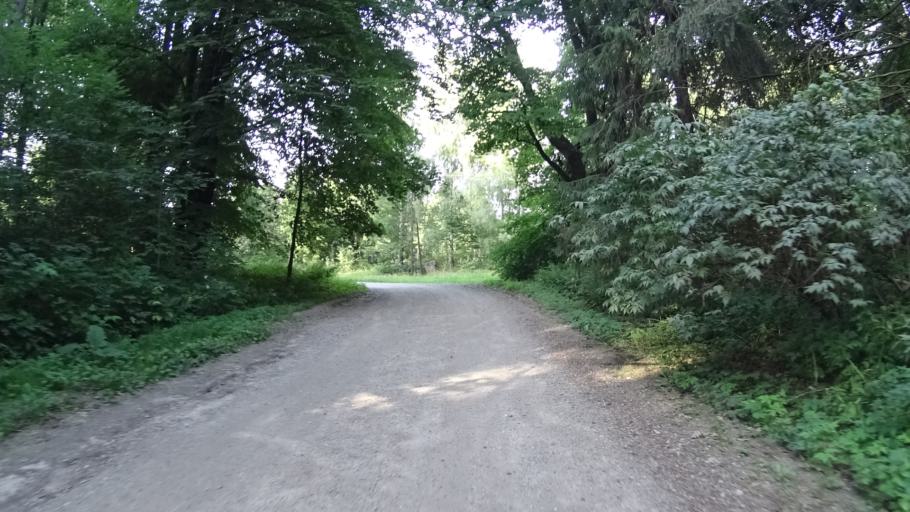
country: FI
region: Uusimaa
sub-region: Helsinki
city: Teekkarikylae
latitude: 60.2487
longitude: 24.8692
